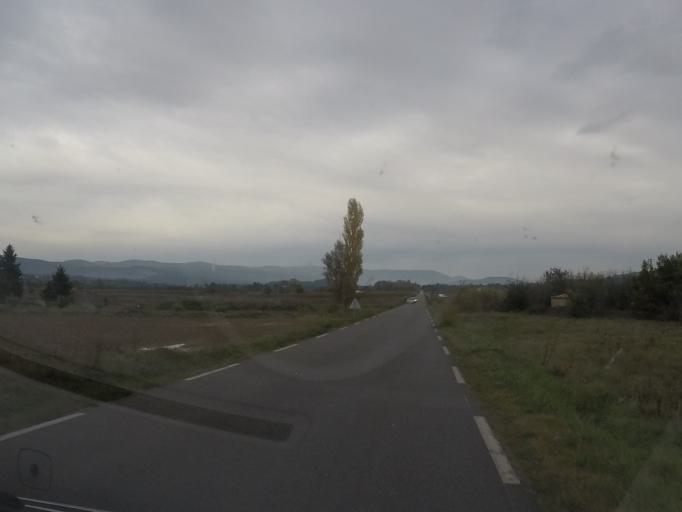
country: FR
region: Provence-Alpes-Cote d'Azur
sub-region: Departement du Vaucluse
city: Gordes
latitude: 43.9123
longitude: 5.2386
